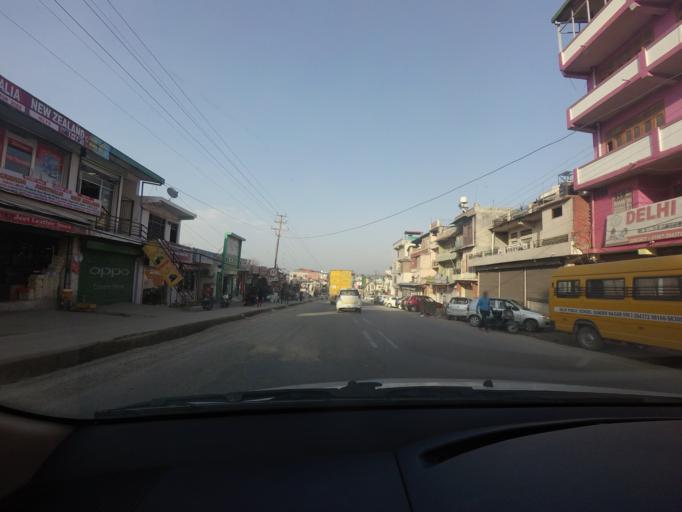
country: IN
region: Himachal Pradesh
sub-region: Mandi
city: Sundarnagar
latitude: 31.5336
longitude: 76.8893
